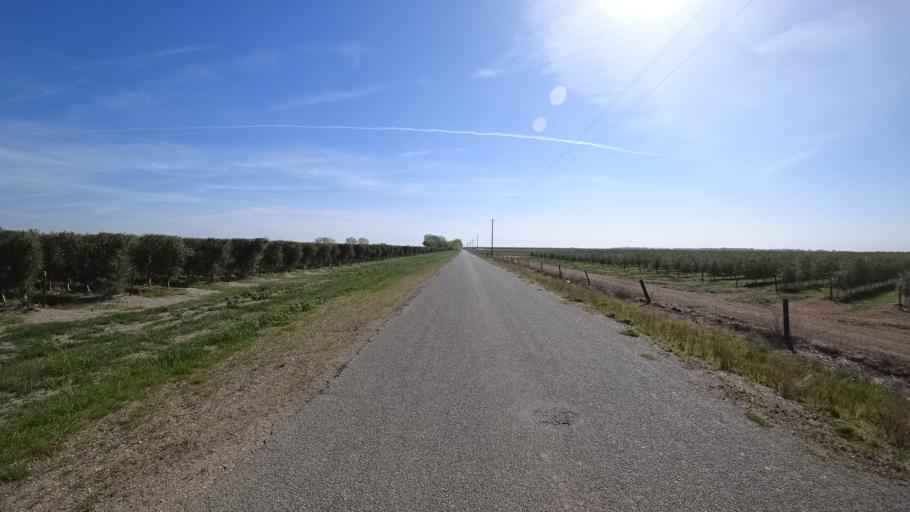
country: US
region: California
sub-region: Glenn County
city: Willows
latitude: 39.6115
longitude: -122.2382
